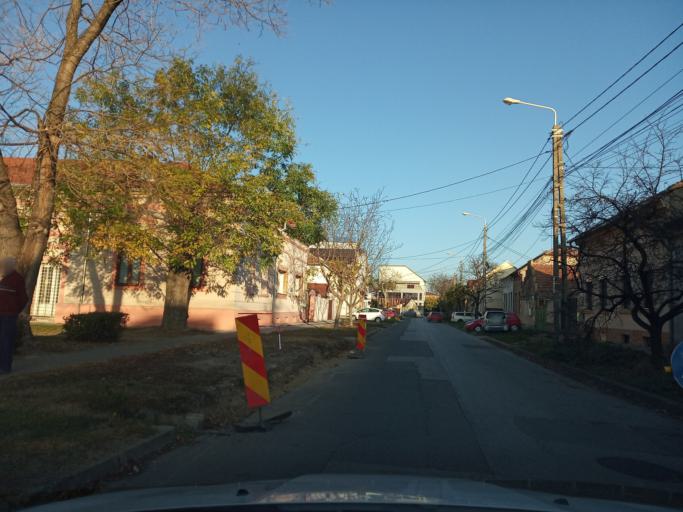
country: RO
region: Timis
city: Timisoara
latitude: 45.7394
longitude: 21.2323
